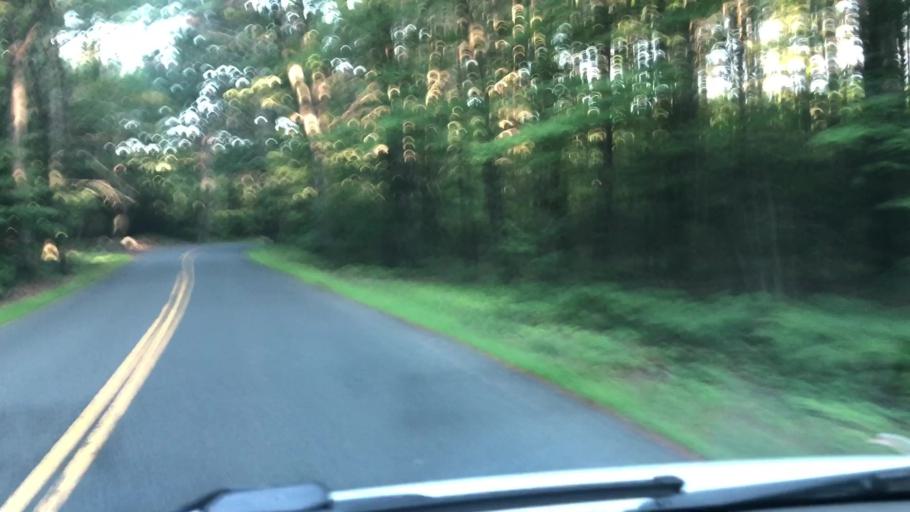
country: US
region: Massachusetts
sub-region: Hampshire County
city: Williamsburg
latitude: 42.3354
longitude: -72.7220
